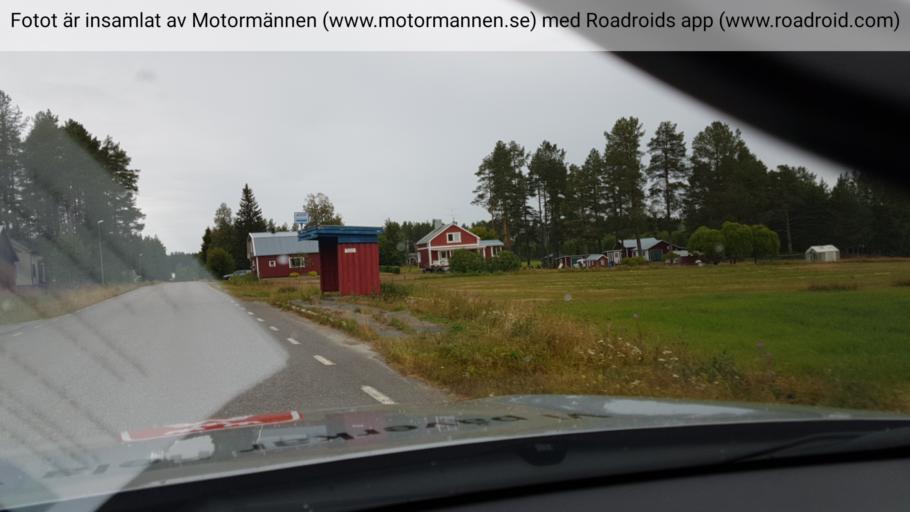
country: SE
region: Norrbotten
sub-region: Bodens Kommun
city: Boden
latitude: 65.8614
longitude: 21.3975
